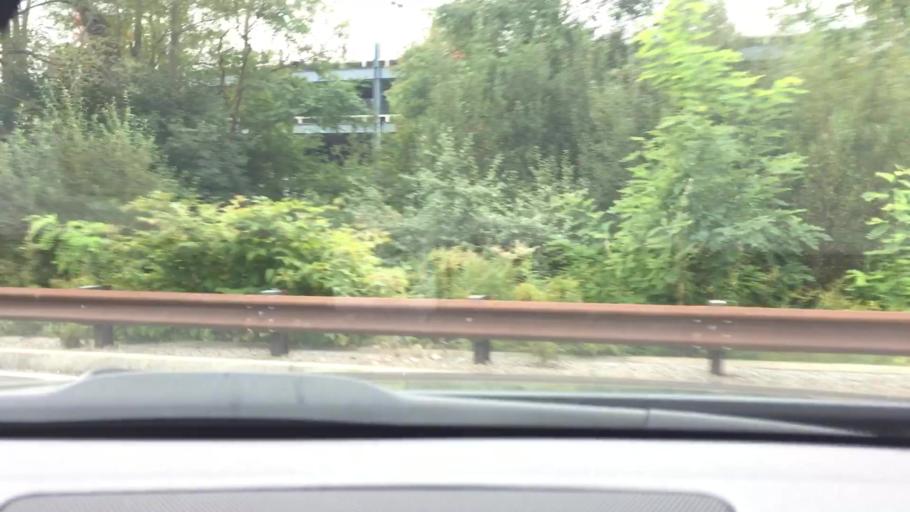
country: US
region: Massachusetts
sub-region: Norfolk County
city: Dedham
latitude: 42.2313
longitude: -71.1753
